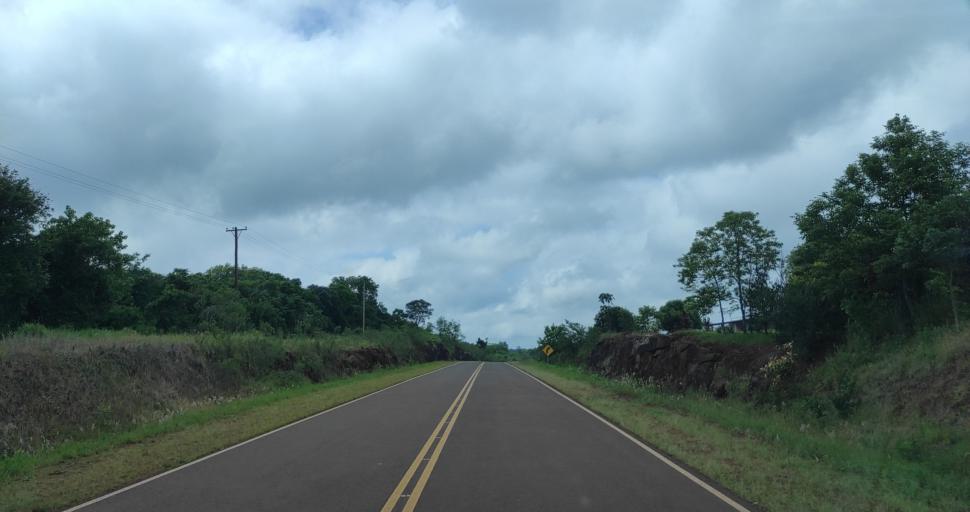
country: AR
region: Misiones
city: Campo Grande
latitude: -27.3283
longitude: -54.8906
